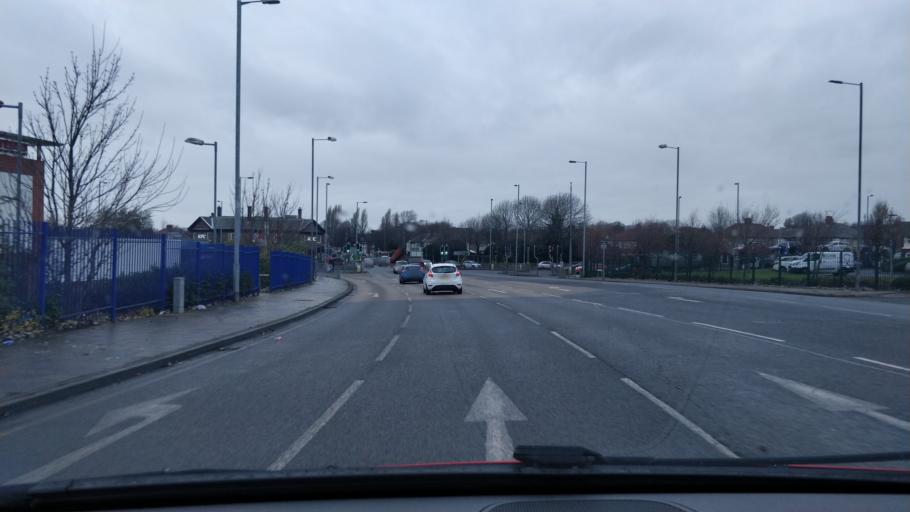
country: GB
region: England
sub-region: Sefton
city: Litherland
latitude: 53.4692
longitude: -2.9967
